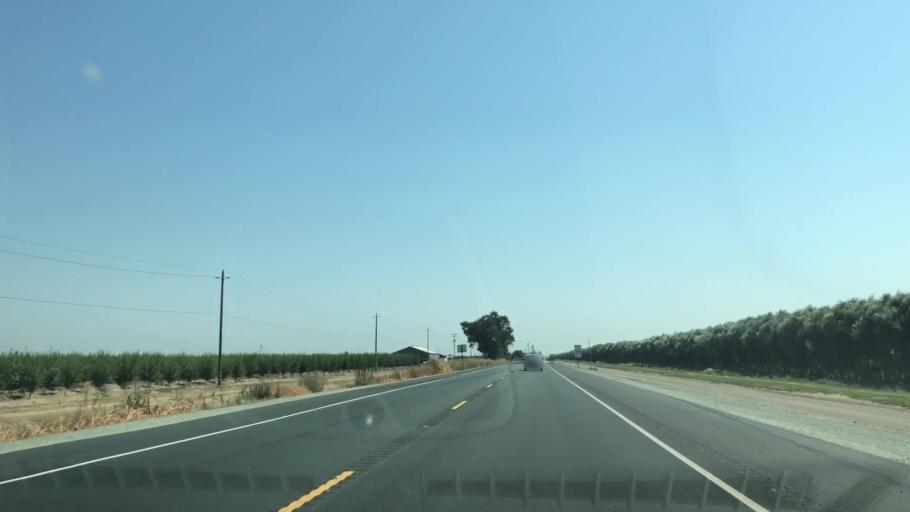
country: US
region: California
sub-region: San Joaquin County
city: Thornton
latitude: 38.1154
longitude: -121.4457
